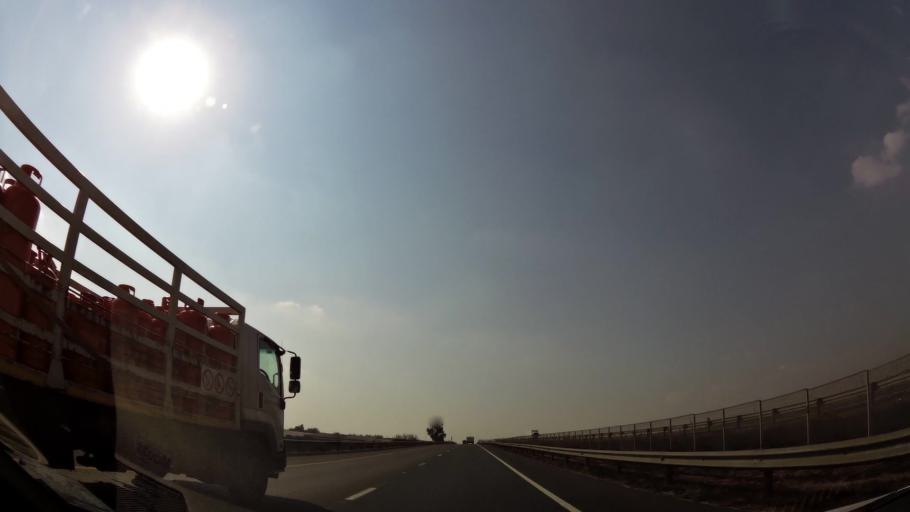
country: ZA
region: Gauteng
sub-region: Ekurhuleni Metropolitan Municipality
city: Brakpan
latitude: -26.1602
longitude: 28.4163
